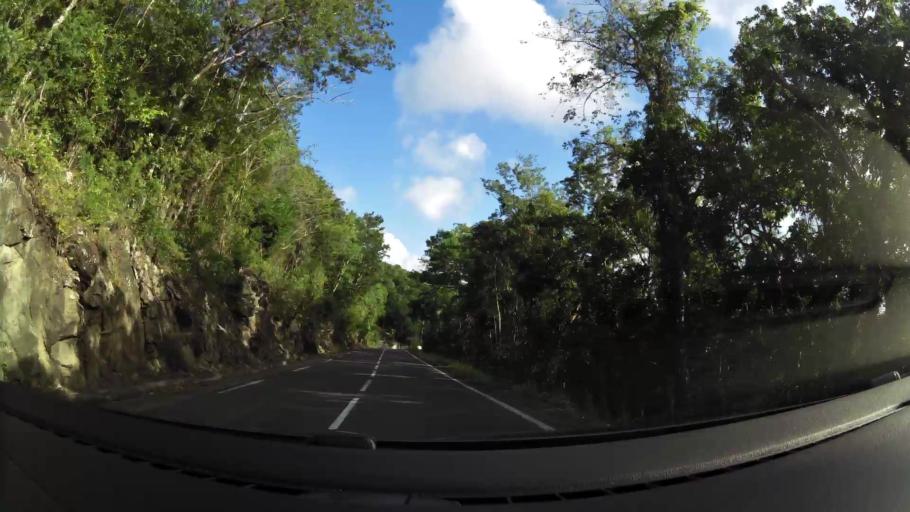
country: GP
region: Guadeloupe
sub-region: Guadeloupe
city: Pointe-Noire
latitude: 16.1999
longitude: -61.7838
